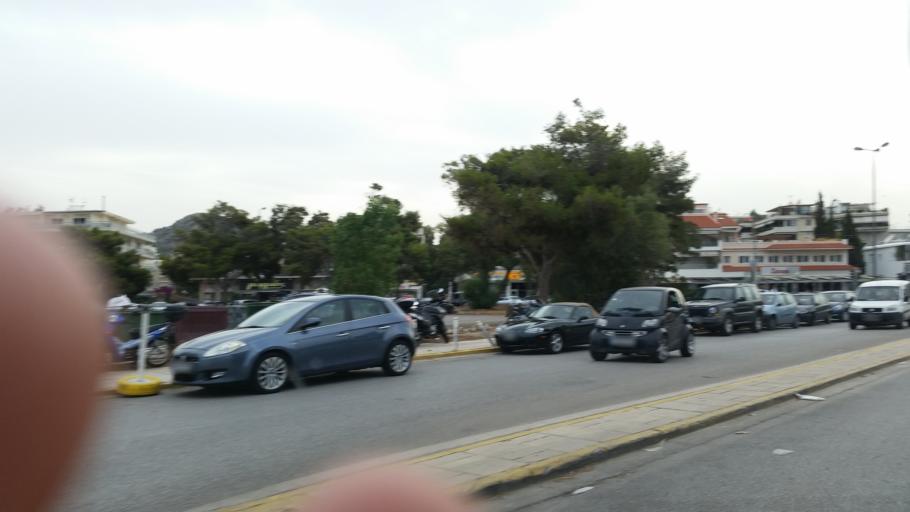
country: GR
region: Attica
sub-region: Nomarchia Anatolikis Attikis
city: Vari
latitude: 37.8206
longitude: 23.8047
